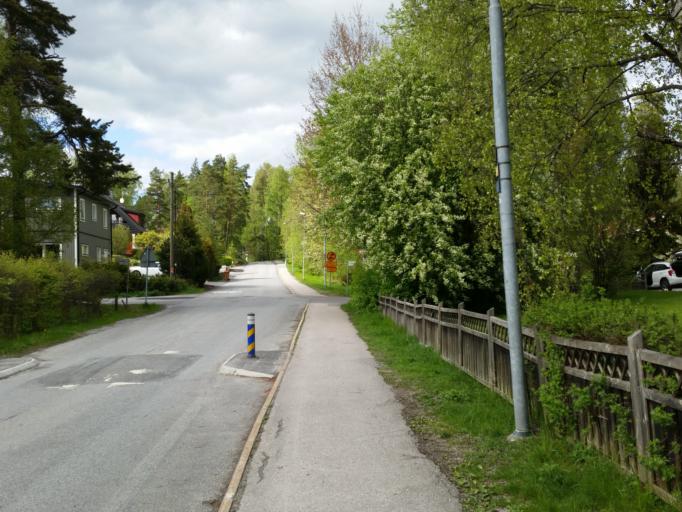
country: SE
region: Stockholm
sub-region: Sollentuna Kommun
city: Sollentuna
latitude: 59.4574
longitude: 17.9498
